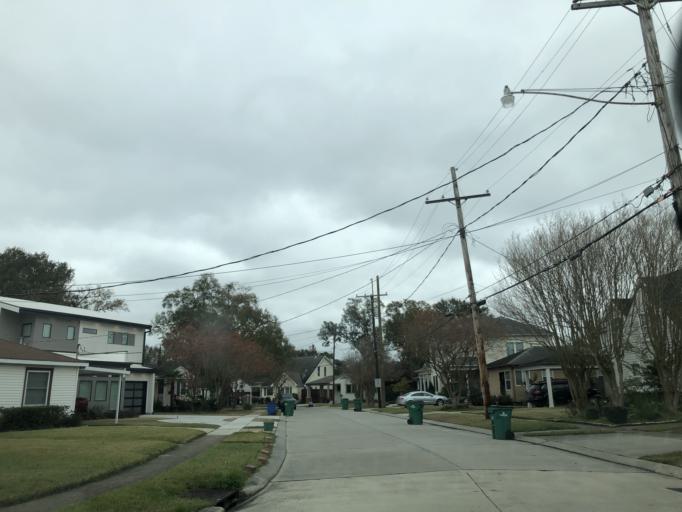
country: US
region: Louisiana
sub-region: Jefferson Parish
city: Metairie
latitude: 29.9756
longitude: -90.1547
